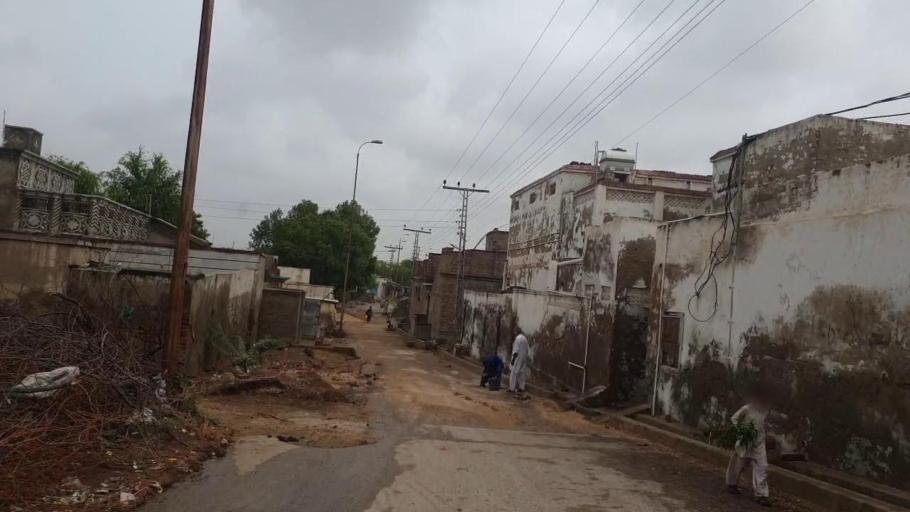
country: PK
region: Sindh
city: Diplo
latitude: 24.4637
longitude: 69.5817
